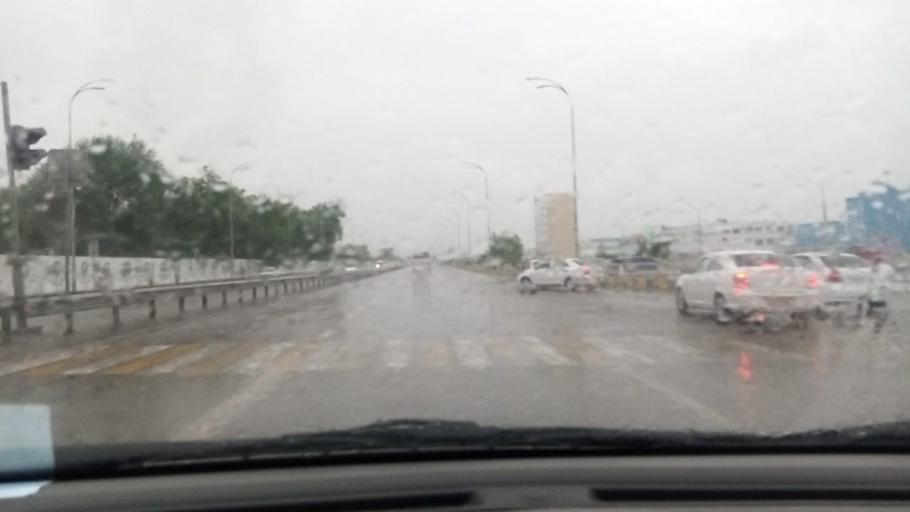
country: UZ
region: Toshkent Shahri
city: Bektemir
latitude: 41.2664
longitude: 69.3684
